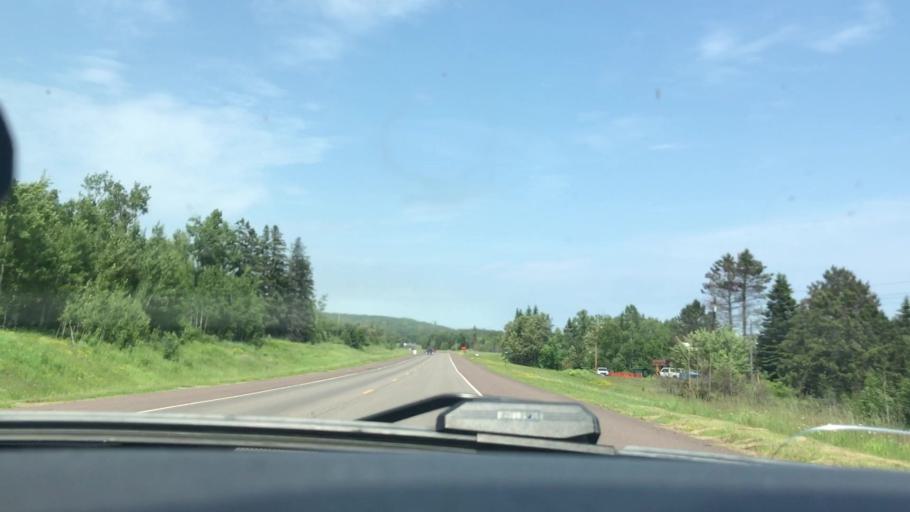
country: US
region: Minnesota
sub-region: Lake County
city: Silver Bay
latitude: 47.3240
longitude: -91.2144
